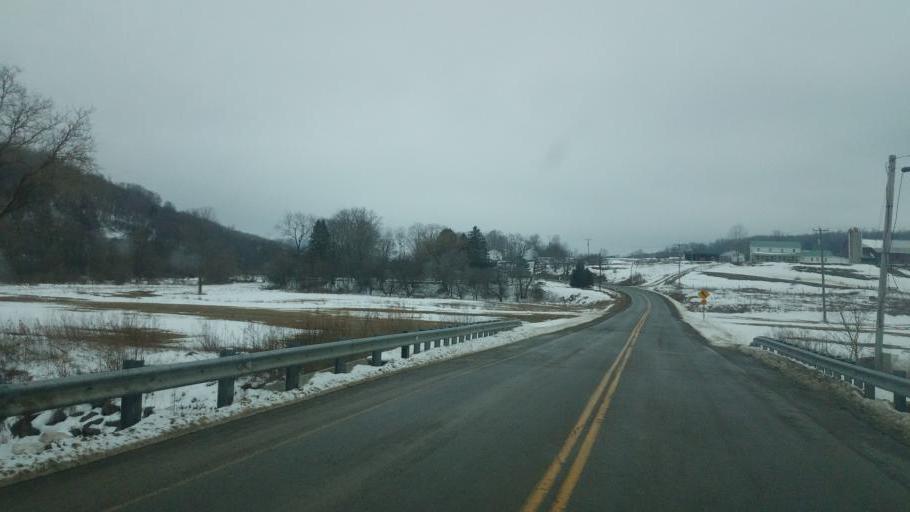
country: US
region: Pennsylvania
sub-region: Tioga County
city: Westfield
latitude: 42.0270
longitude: -77.5353
